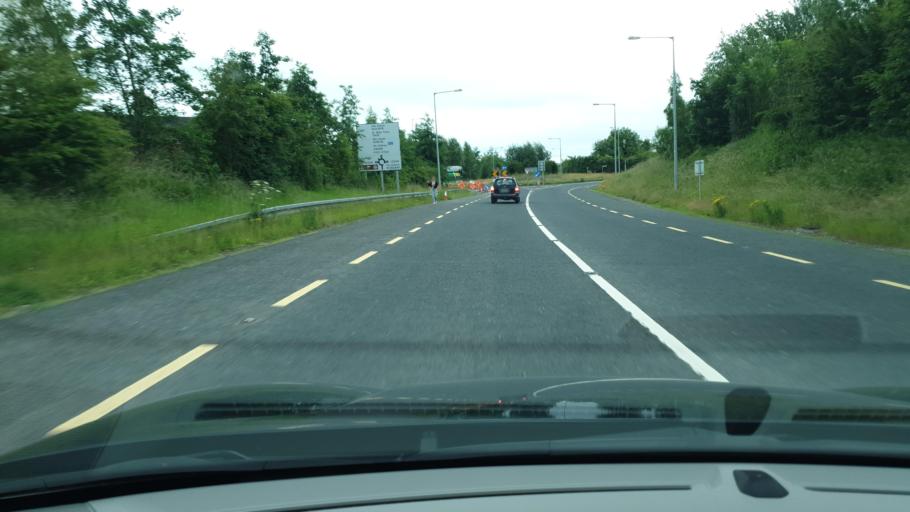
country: IE
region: Leinster
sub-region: An Mhi
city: Dunshaughlin
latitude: 53.5169
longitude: -6.5544
